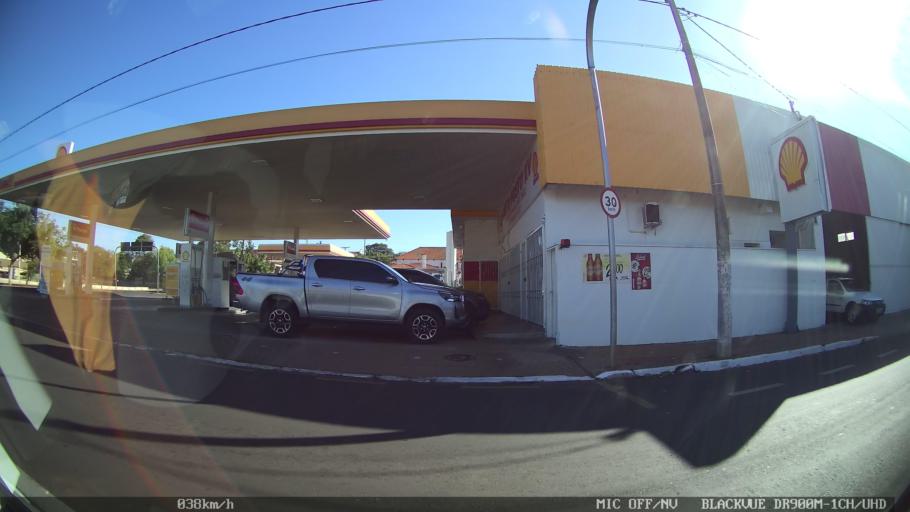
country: BR
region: Sao Paulo
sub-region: Olimpia
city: Olimpia
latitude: -20.7402
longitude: -48.9103
